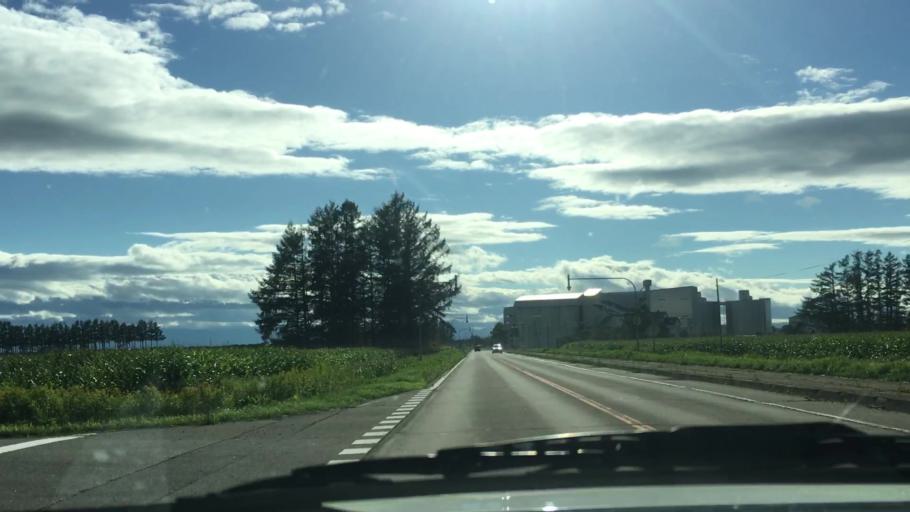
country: JP
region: Hokkaido
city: Otofuke
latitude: 43.1639
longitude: 143.2586
